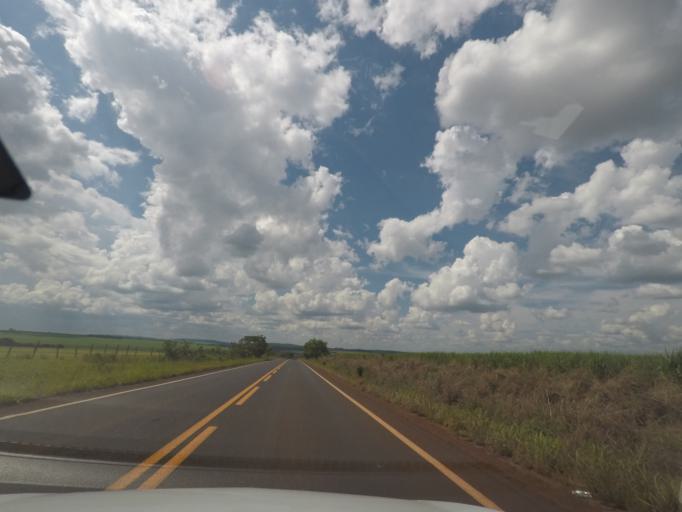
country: BR
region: Minas Gerais
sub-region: Conceicao Das Alagoas
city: Conceicao das Alagoas
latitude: -19.8270
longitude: -48.5918
